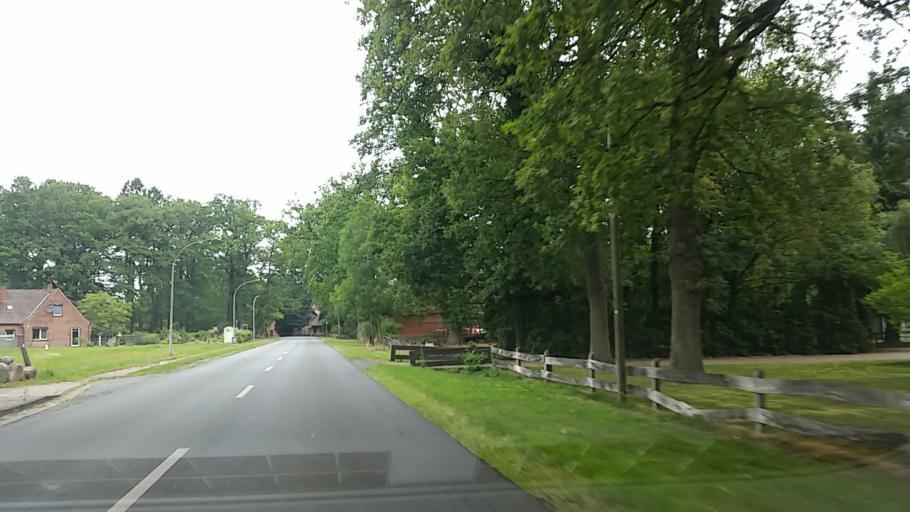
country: DE
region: Lower Saxony
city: Vollersode
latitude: 53.4118
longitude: 8.9154
